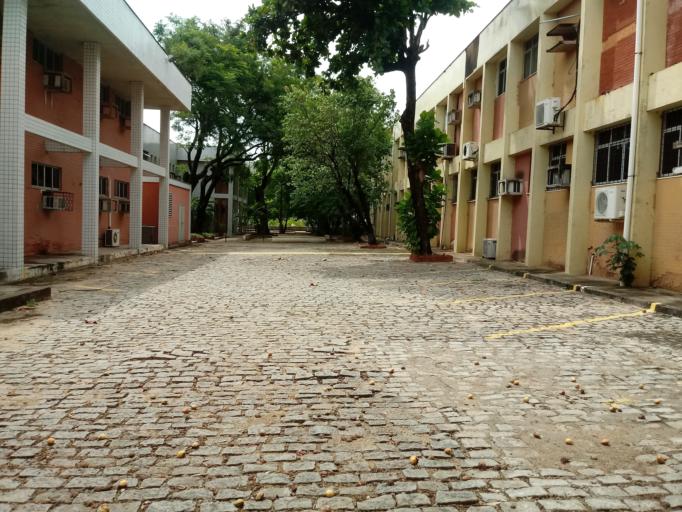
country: BR
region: Ceara
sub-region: Fortaleza
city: Fortaleza
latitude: -3.7448
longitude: -38.5750
